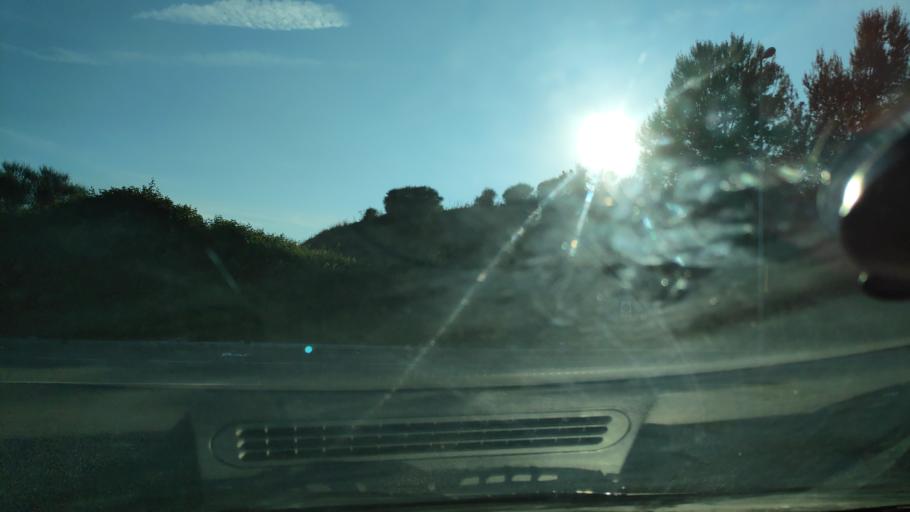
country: ES
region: Catalonia
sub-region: Provincia de Barcelona
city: Terrassa
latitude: 41.5399
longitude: 2.0302
